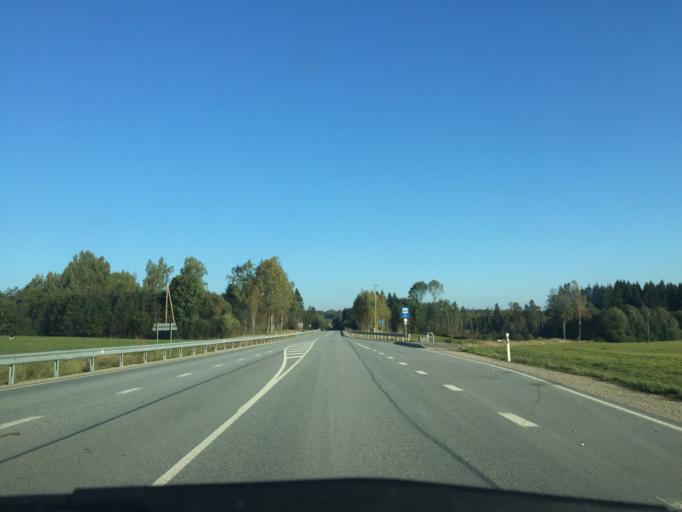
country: LV
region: Raunas
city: Rauna
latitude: 57.1771
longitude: 25.6220
